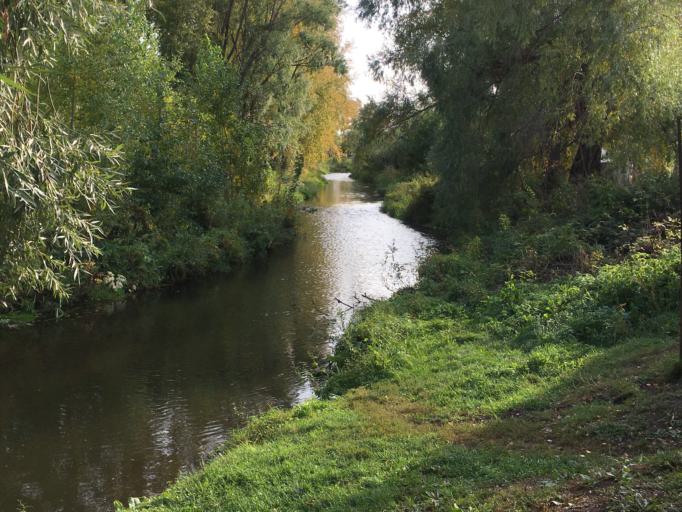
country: RU
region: Bashkortostan
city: Meleuz
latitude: 52.9594
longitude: 55.9213
